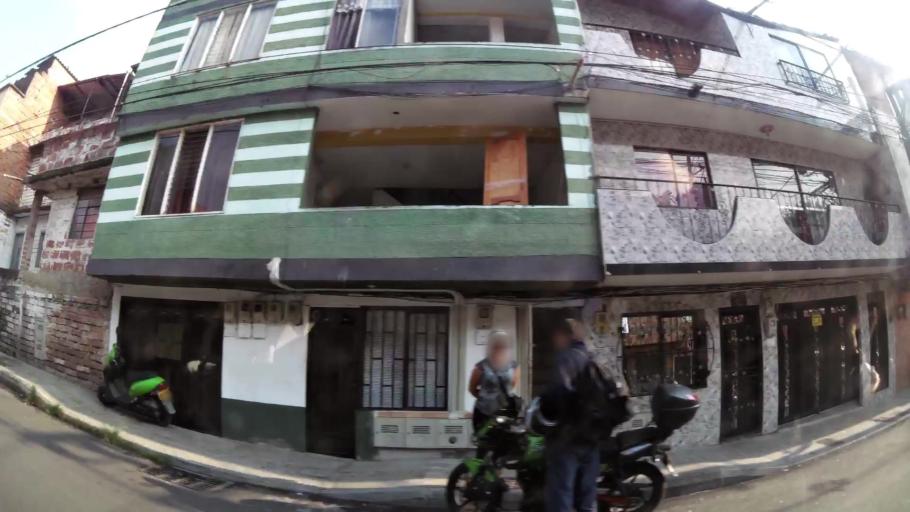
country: CO
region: Antioquia
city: Sabaneta
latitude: 6.1630
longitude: -75.6219
